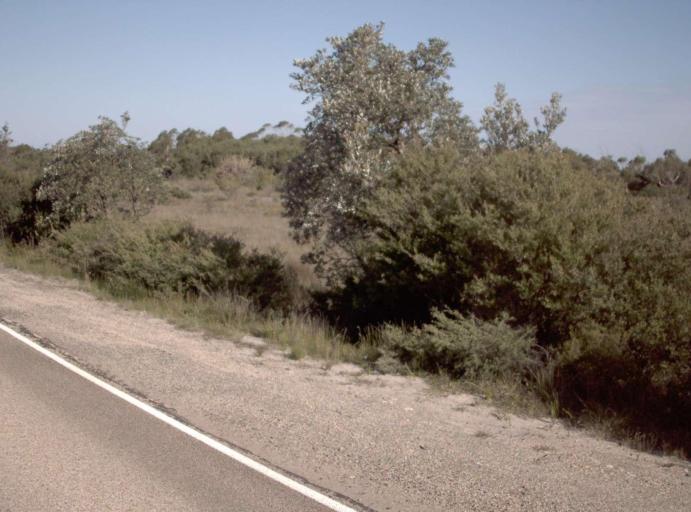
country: AU
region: Victoria
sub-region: East Gippsland
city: Lakes Entrance
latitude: -37.8024
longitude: 148.6277
